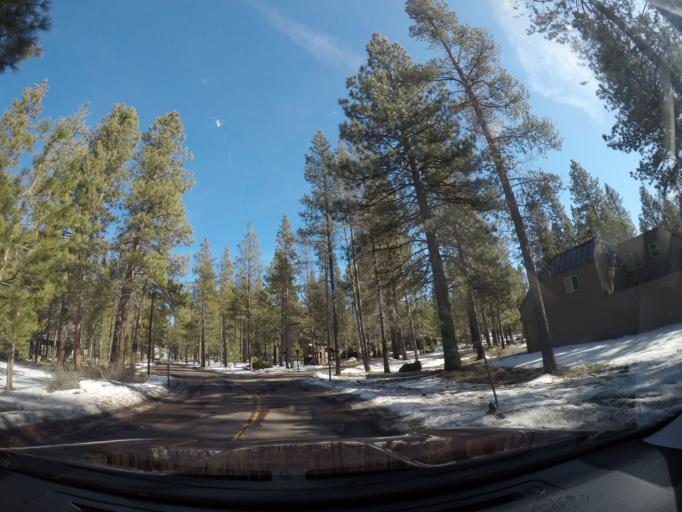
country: US
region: Oregon
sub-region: Deschutes County
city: Sunriver
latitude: 43.8715
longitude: -121.4342
